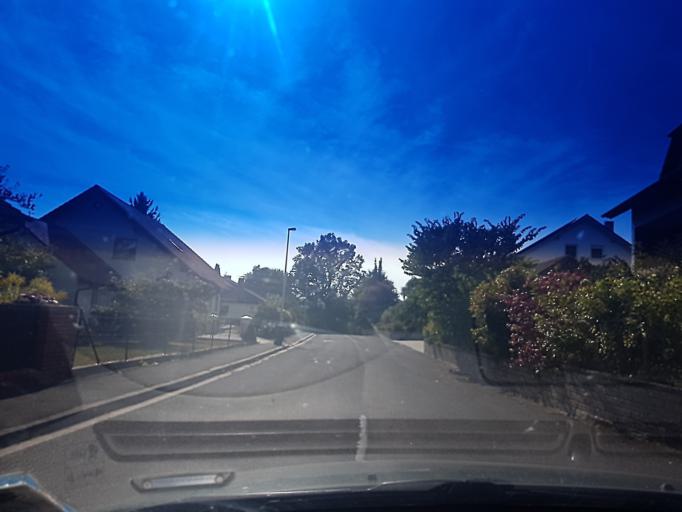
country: DE
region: Bavaria
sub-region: Upper Franconia
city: Schlusselfeld
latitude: 49.7639
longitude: 10.6219
